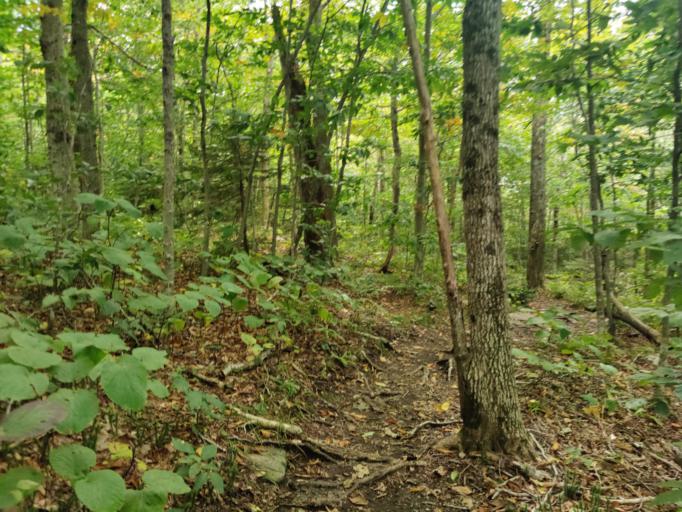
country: US
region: Vermont
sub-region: Bennington County
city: Manchester Center
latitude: 43.2633
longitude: -72.9397
